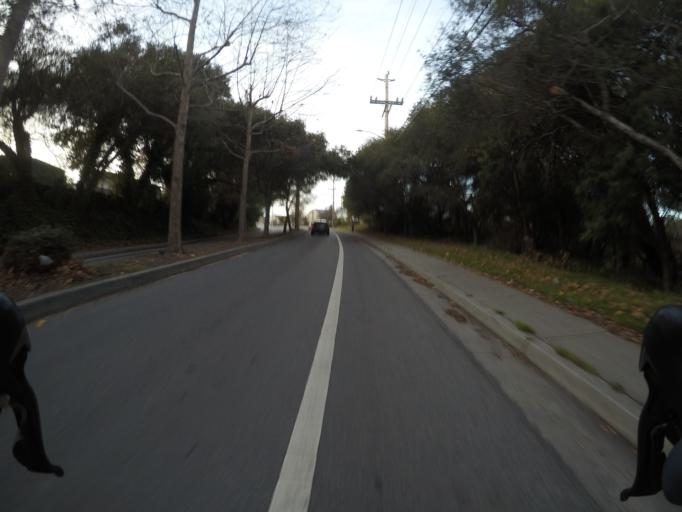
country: US
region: California
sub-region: Santa Cruz County
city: Live Oak
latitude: 36.9746
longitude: -121.9752
